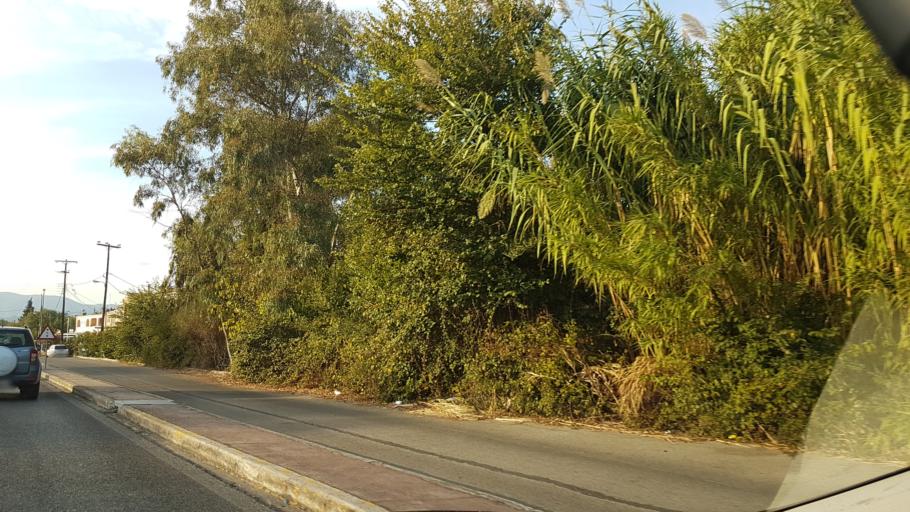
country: GR
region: Ionian Islands
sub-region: Nomos Kerkyras
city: Kontokali
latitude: 39.6467
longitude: 19.8479
